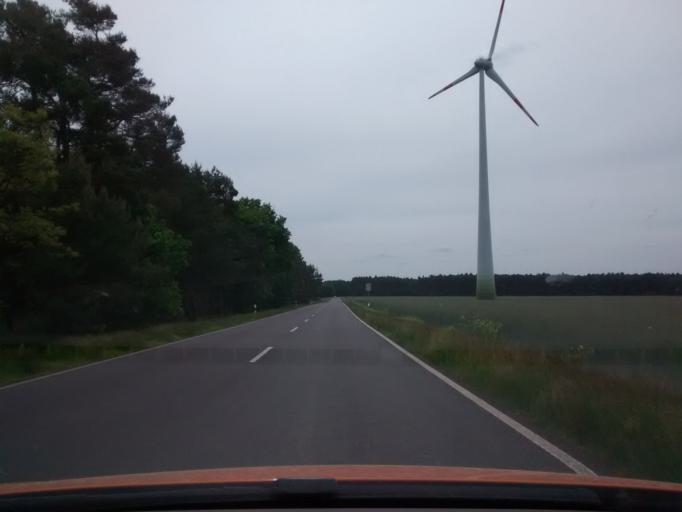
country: DE
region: Saxony-Anhalt
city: Holzdorf
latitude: 51.8587
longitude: 13.1467
